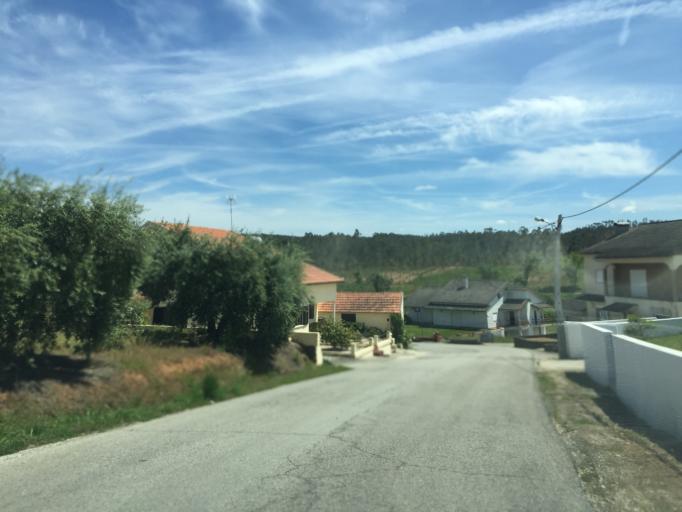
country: PT
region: Coimbra
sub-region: Soure
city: Soure
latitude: 40.0520
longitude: -8.6715
